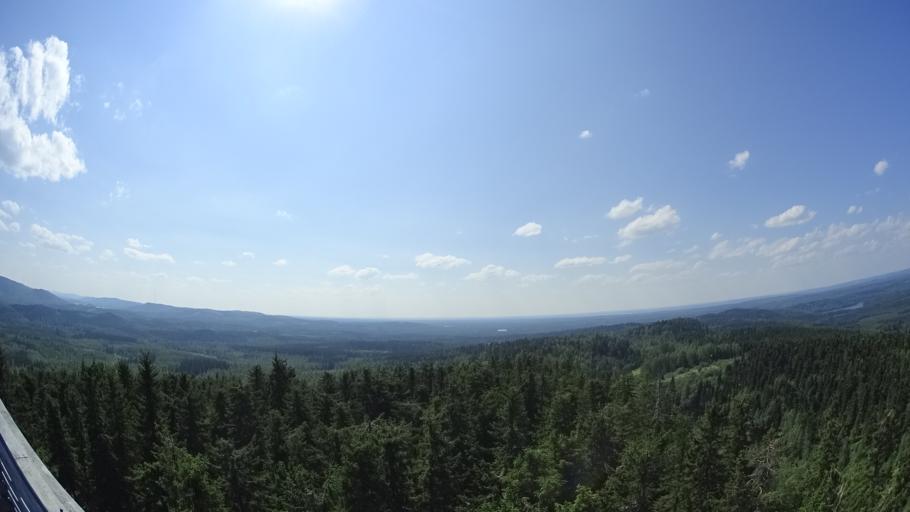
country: FI
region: North Karelia
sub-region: Pielisen Karjala
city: Lieksa
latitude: 63.1287
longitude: 29.7275
